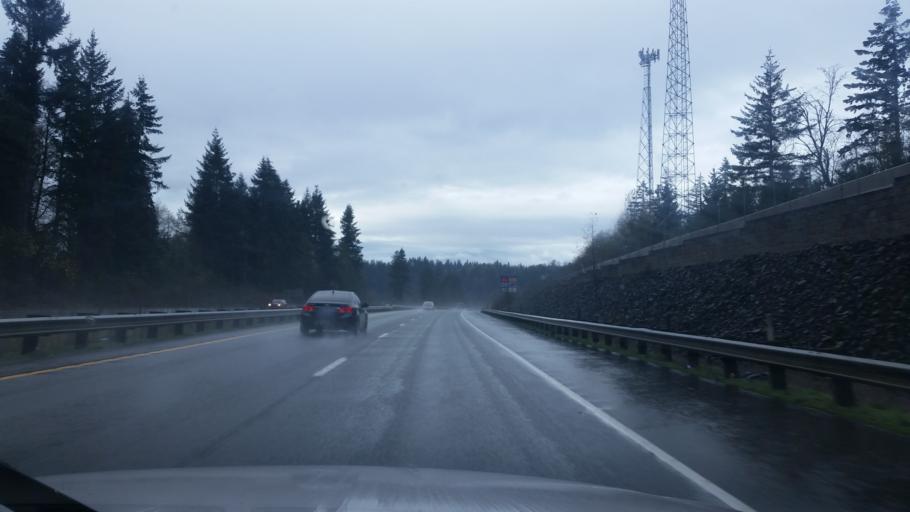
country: US
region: Washington
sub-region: King County
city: Maple Valley
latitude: 47.4105
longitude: -122.0297
